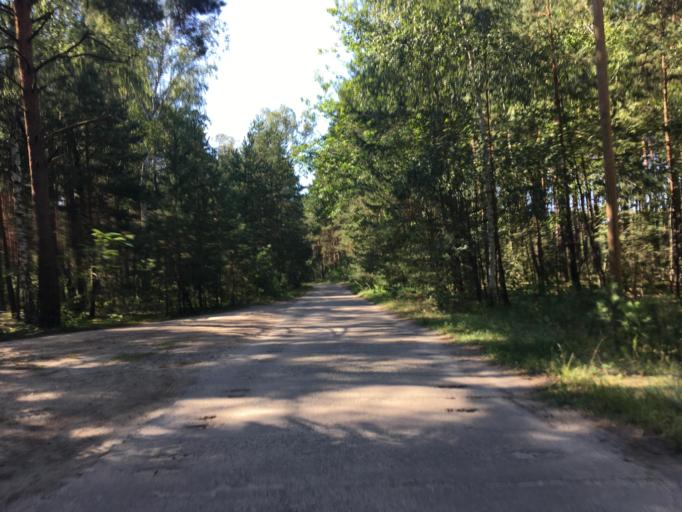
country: DE
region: Brandenburg
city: Gross Koris
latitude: 52.1896
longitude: 13.7146
